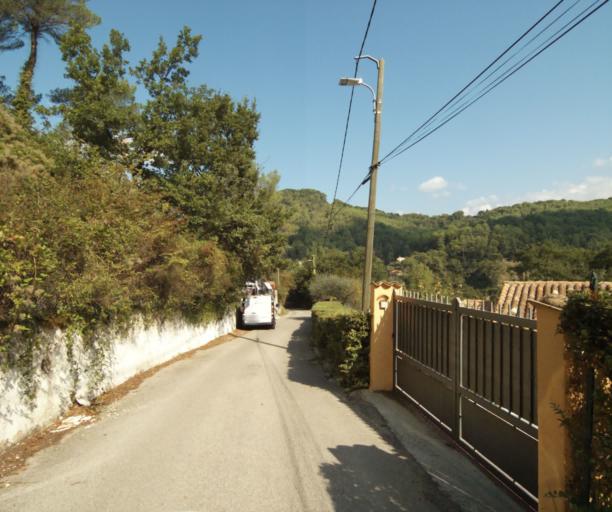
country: FR
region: Provence-Alpes-Cote d'Azur
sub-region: Departement des Alpes-Maritimes
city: Drap
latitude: 43.7632
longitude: 7.3420
